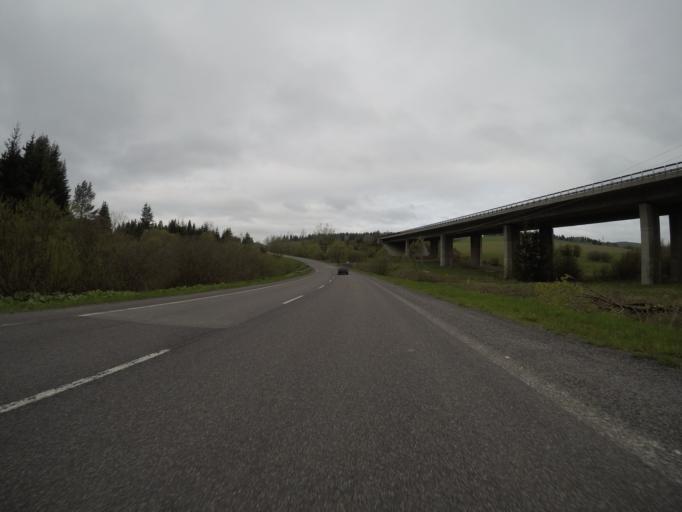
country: SK
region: Zilinsky
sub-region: Okres Liptovsky Mikulas
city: Hybe
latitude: 49.0644
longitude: 19.9469
